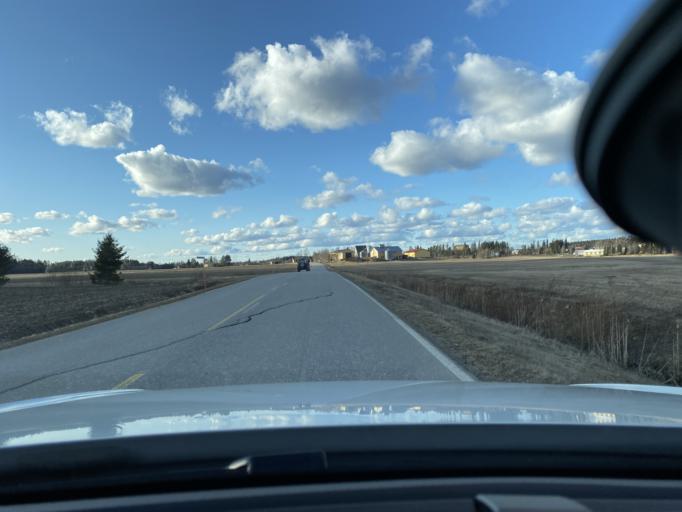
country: FI
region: Pirkanmaa
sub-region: Lounais-Pirkanmaa
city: Punkalaidun
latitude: 61.1010
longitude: 23.1203
